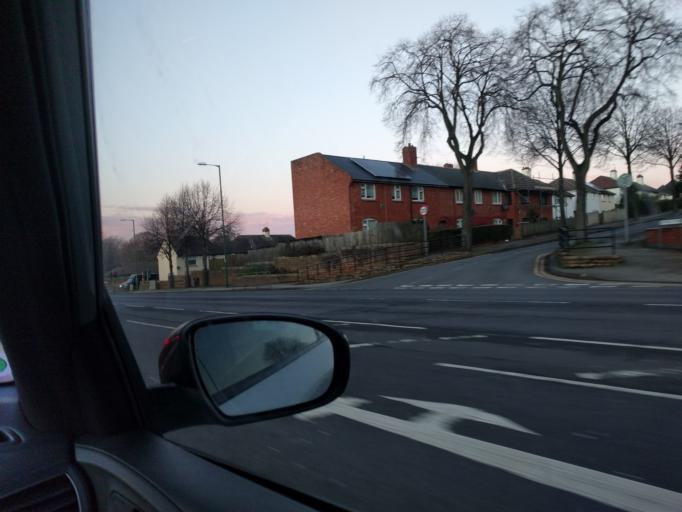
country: GB
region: England
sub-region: Nottingham
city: Nottingham
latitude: 52.9812
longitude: -1.1949
